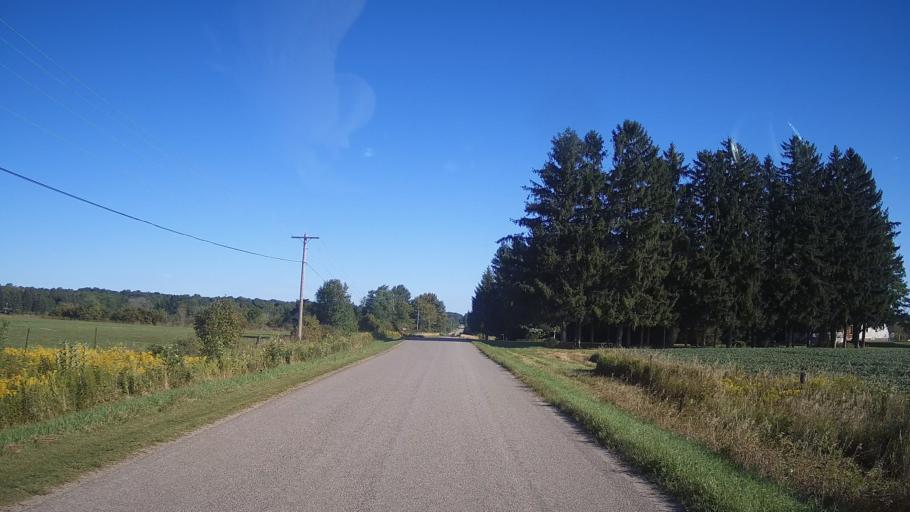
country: US
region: New York
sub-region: Jefferson County
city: Alexandria Bay
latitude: 44.4287
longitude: -75.9802
